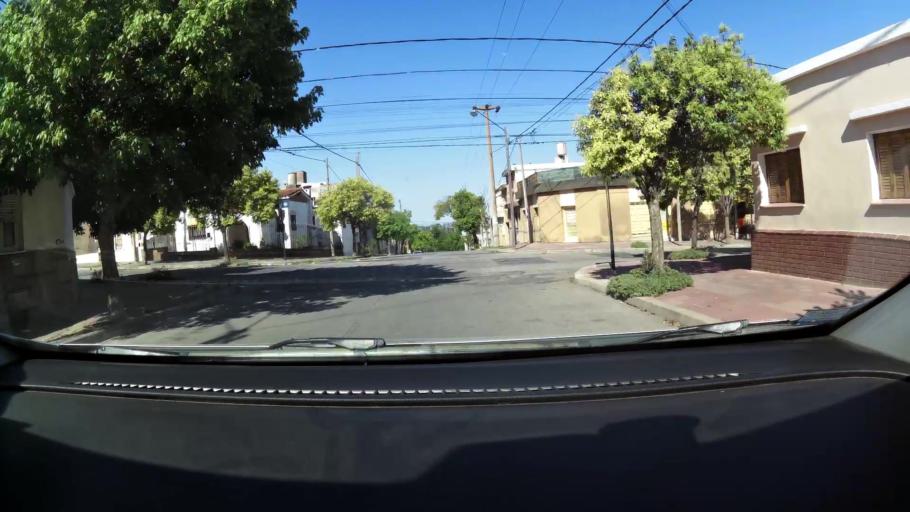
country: AR
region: Cordoba
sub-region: Departamento de Capital
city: Cordoba
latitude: -31.4056
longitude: -64.1525
